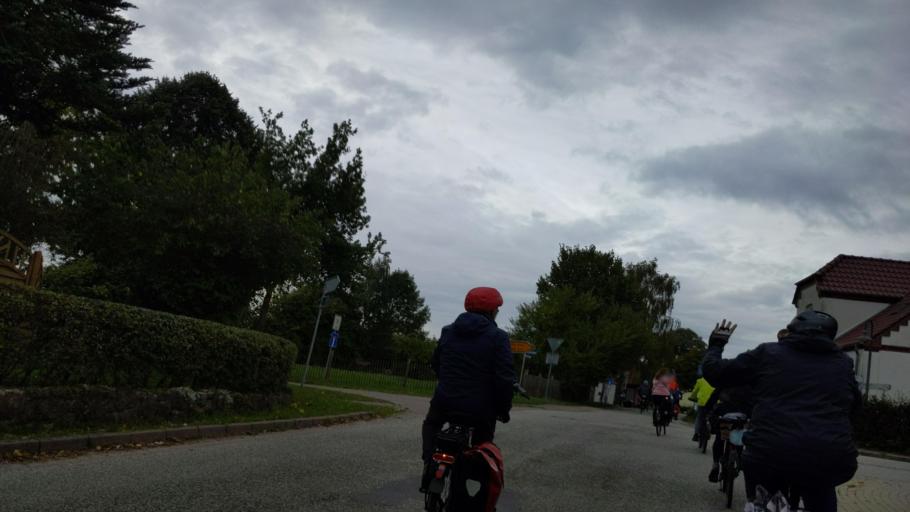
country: DE
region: Schleswig-Holstein
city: Gross Sarau
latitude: 53.7684
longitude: 10.7692
